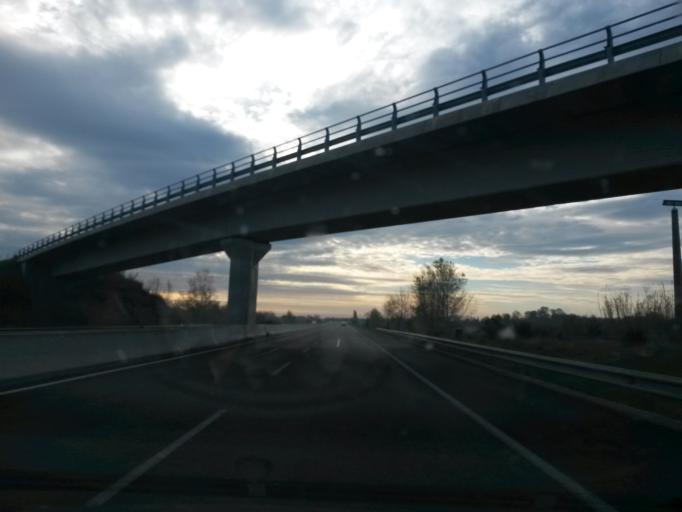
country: ES
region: Catalonia
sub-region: Provincia de Girona
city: Vila-sacra
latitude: 42.2680
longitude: 3.0250
